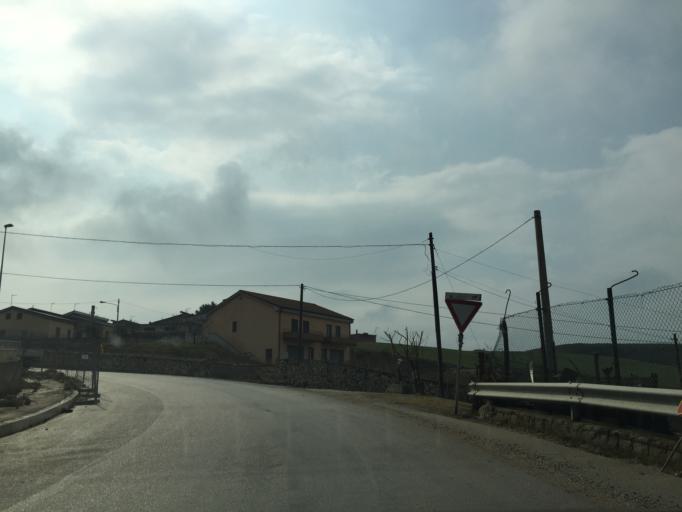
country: IT
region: Apulia
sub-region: Provincia di Foggia
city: Troia
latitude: 41.3593
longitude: 15.3017
